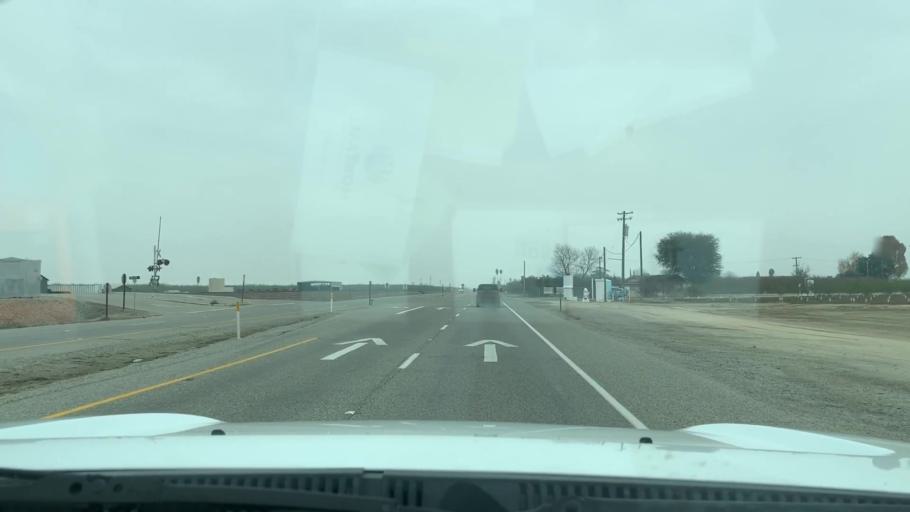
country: US
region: California
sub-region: Kern County
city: Shafter
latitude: 35.5212
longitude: -119.2966
